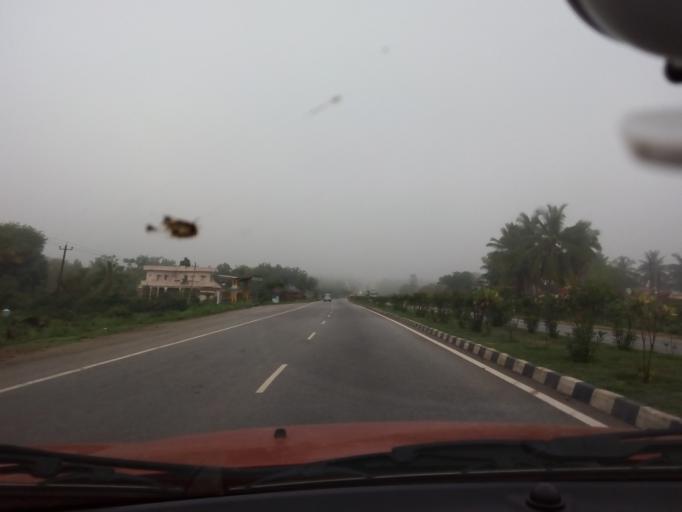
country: IN
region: Karnataka
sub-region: Tumkur
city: Kunigal
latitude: 13.0406
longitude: 77.1095
